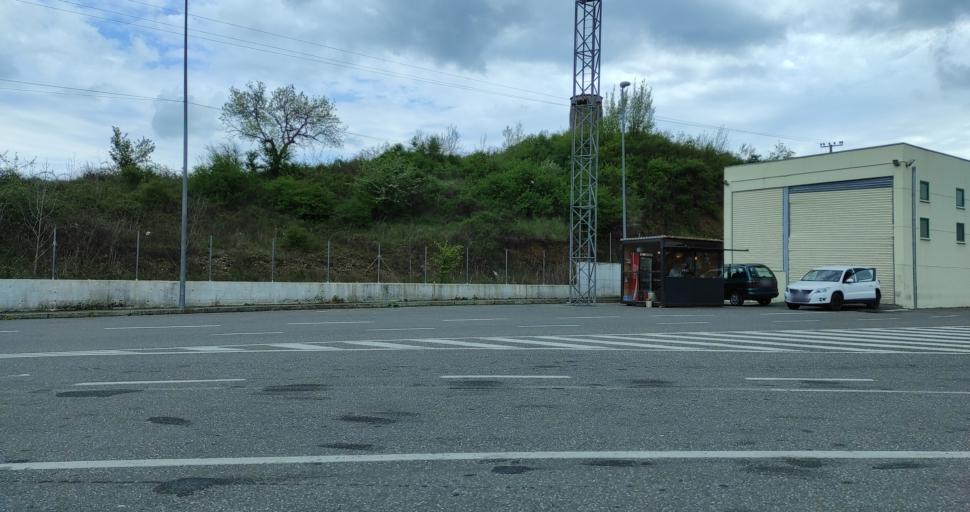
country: AL
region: Shkoder
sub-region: Rrethi i Shkodres
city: Dajc
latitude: 42.0172
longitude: 19.3730
